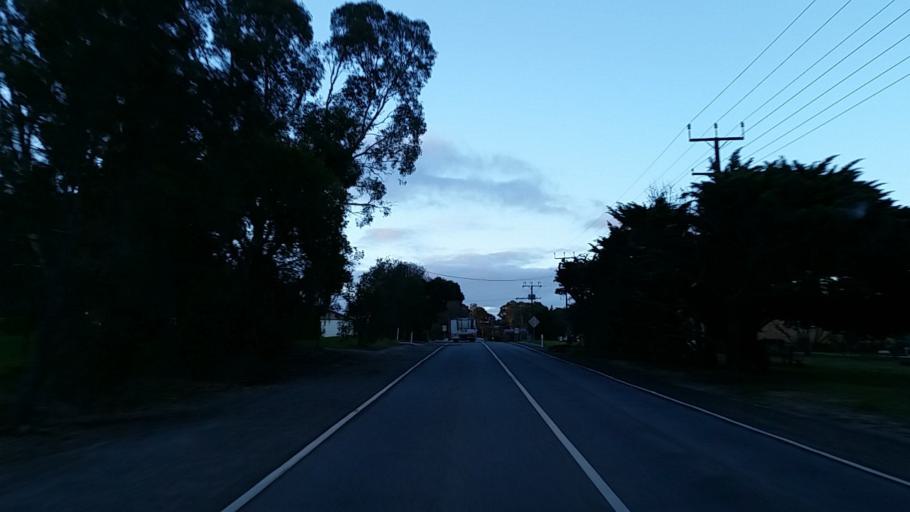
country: AU
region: South Australia
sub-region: Barossa
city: Williamstown
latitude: -34.6774
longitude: 138.8858
